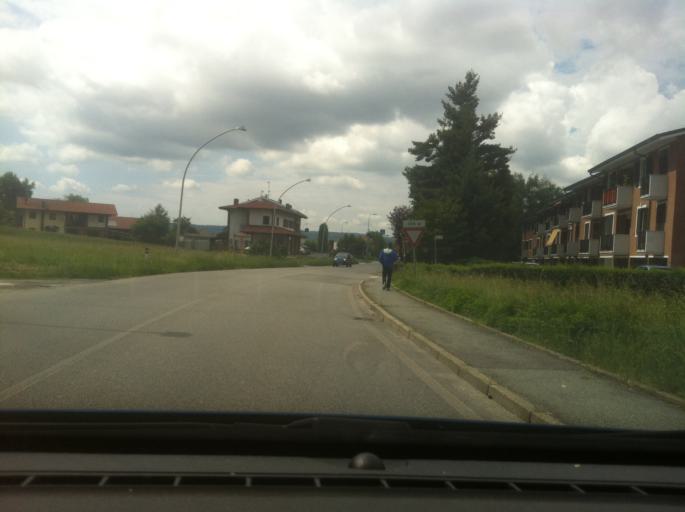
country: IT
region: Piedmont
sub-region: Provincia di Torino
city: Pavone Canavese
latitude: 45.4455
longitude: 7.8569
